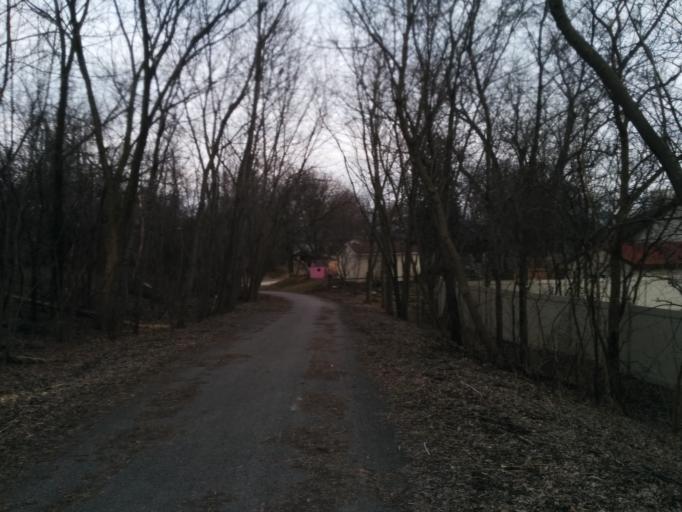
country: US
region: Illinois
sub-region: DuPage County
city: Lombard
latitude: 41.8914
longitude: -88.0211
